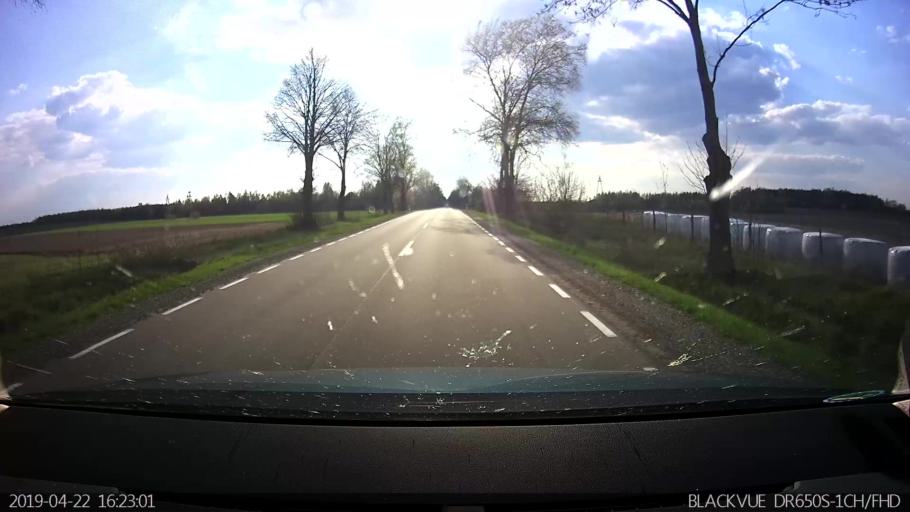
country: PL
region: Podlasie
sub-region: Powiat hajnowski
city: Kleszczele
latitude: 52.5606
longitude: 23.2957
